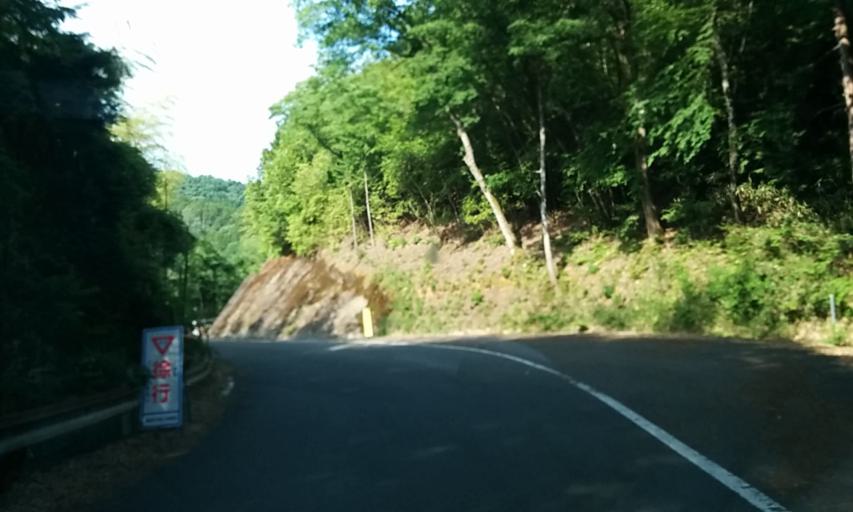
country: JP
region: Kyoto
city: Ayabe
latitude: 35.3529
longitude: 135.2006
